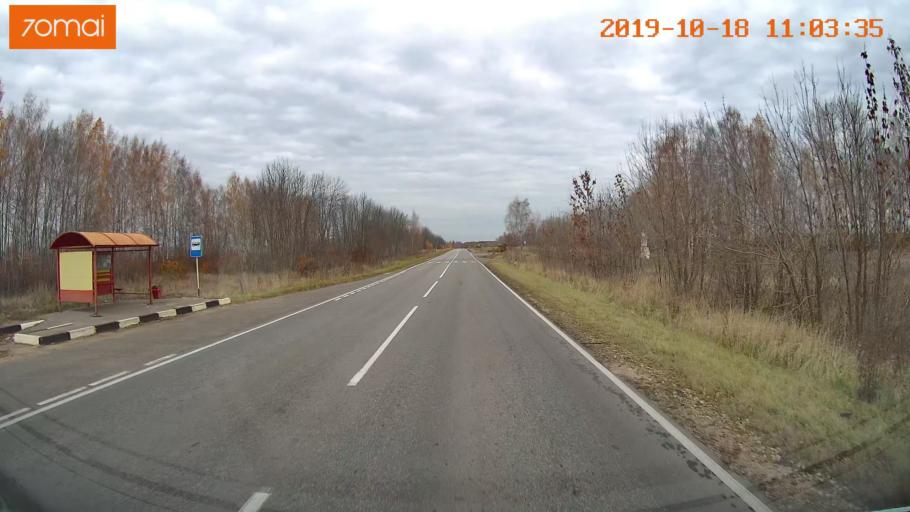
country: RU
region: Tula
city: Yepifan'
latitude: 53.8820
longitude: 38.5490
